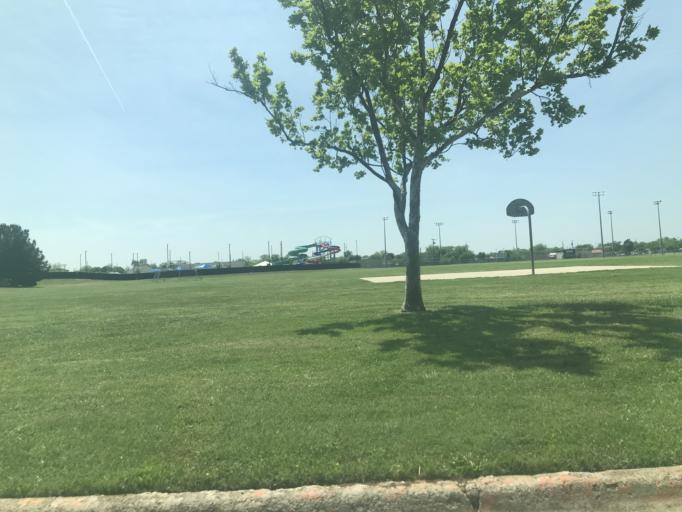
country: US
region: Texas
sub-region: Taylor County
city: Abilene
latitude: 32.4422
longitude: -99.7563
